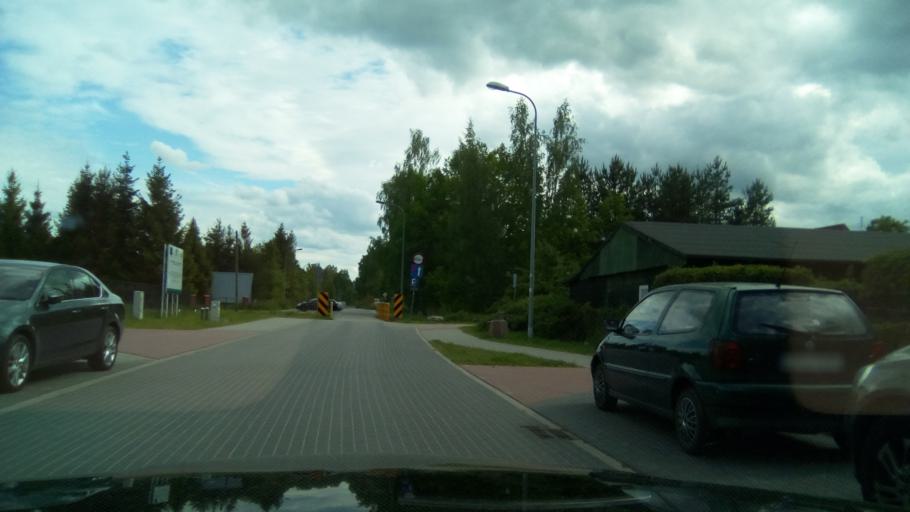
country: PL
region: Pomeranian Voivodeship
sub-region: Powiat pucki
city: Wierzchucino
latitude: 54.8276
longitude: 18.0764
